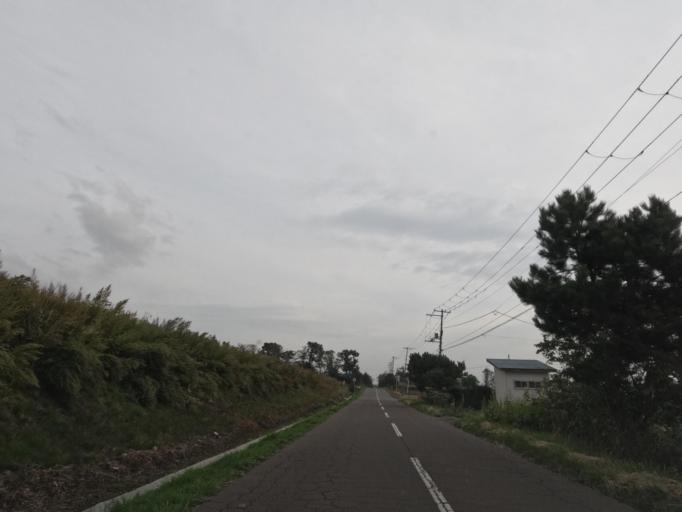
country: JP
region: Hokkaido
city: Date
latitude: 42.4353
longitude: 140.9080
